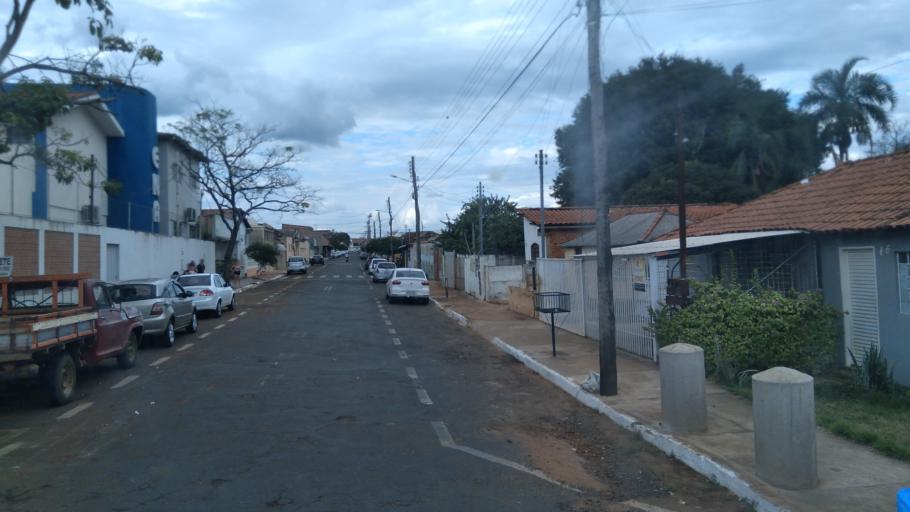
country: BR
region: Goias
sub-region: Mineiros
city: Mineiros
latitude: -17.5714
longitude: -52.5602
